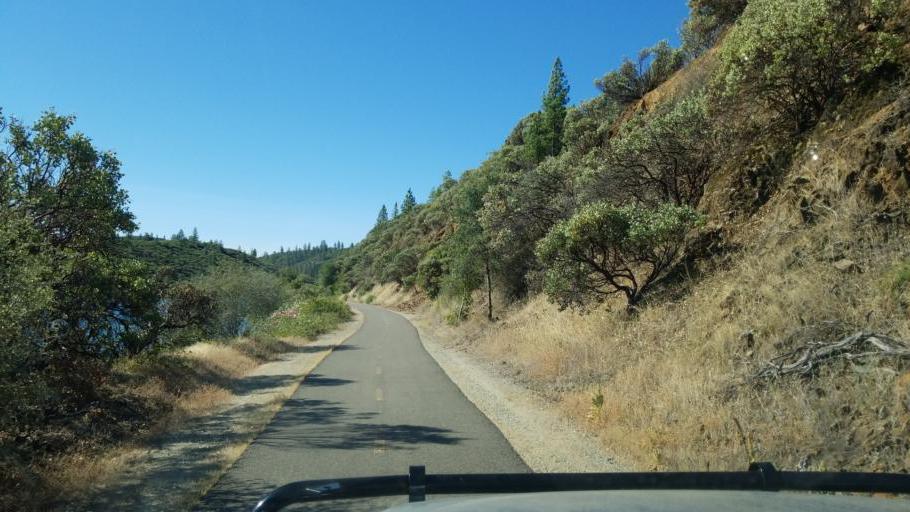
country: US
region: California
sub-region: Shasta County
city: Shasta
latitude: 40.6696
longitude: -122.4611
